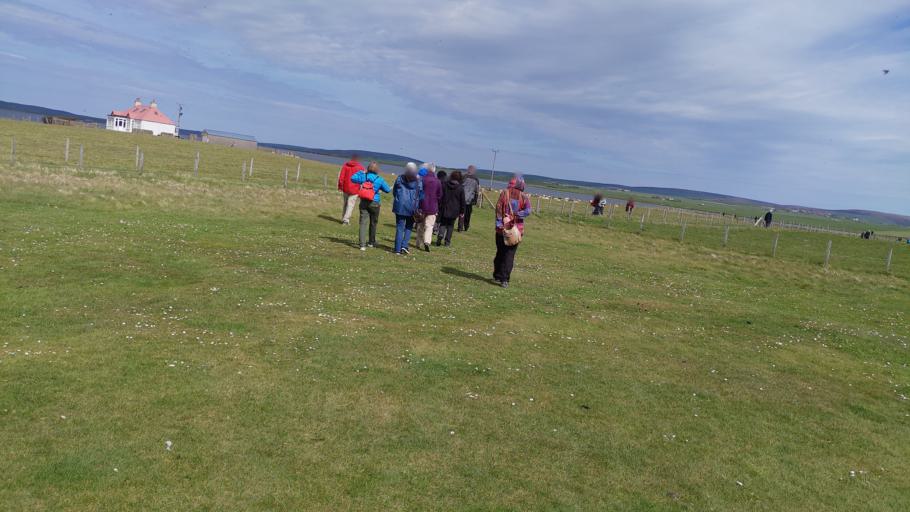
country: GB
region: Scotland
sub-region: Orkney Islands
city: Stromness
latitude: 58.9942
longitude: -3.2081
